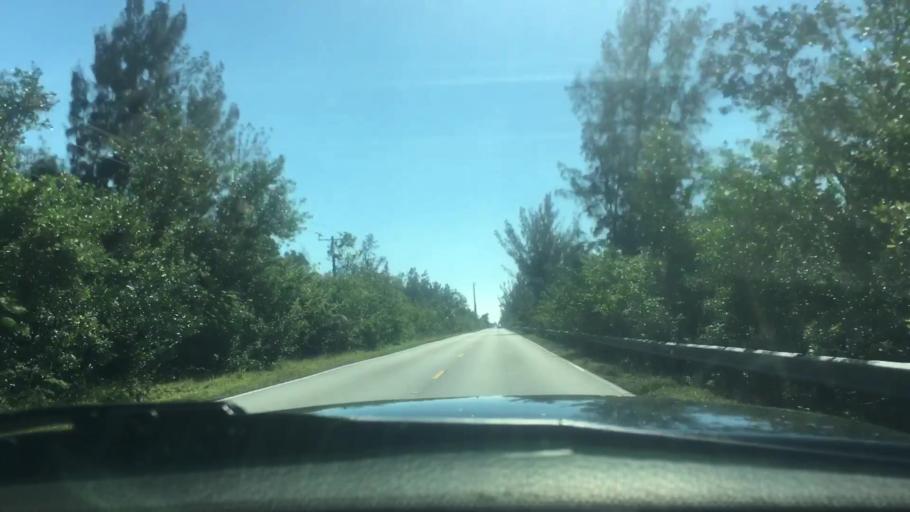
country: US
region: Florida
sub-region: Miami-Dade County
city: Florida City
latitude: 25.3665
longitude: -80.4296
